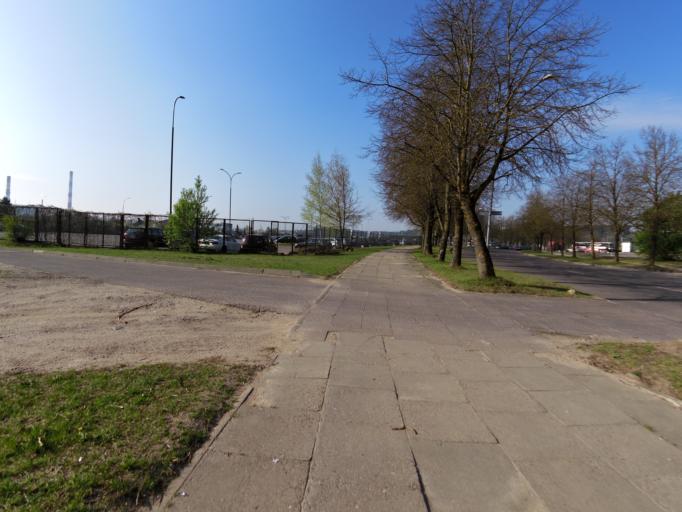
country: LT
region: Vilnius County
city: Lazdynai
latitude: 54.6737
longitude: 25.2270
